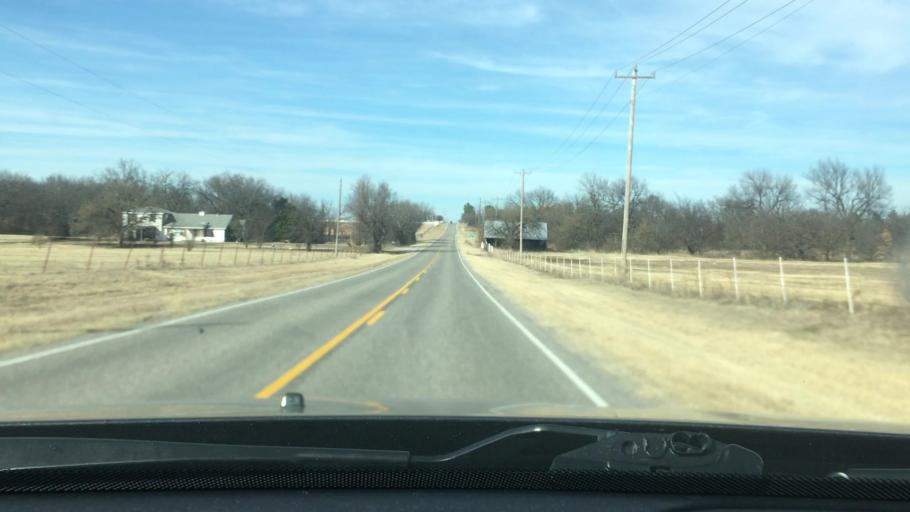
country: US
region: Oklahoma
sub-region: Murray County
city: Davis
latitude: 34.4889
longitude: -97.0905
